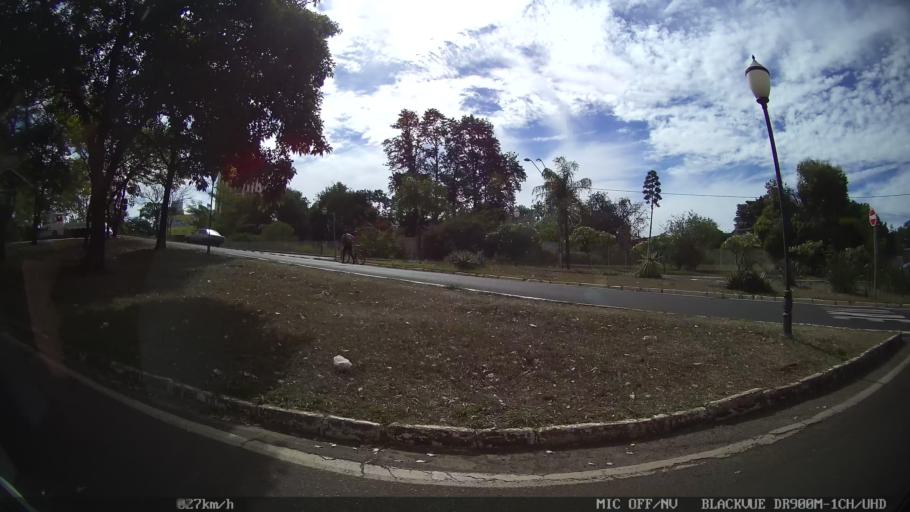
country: BR
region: Sao Paulo
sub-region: Catanduva
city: Catanduva
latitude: -21.1375
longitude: -48.9665
